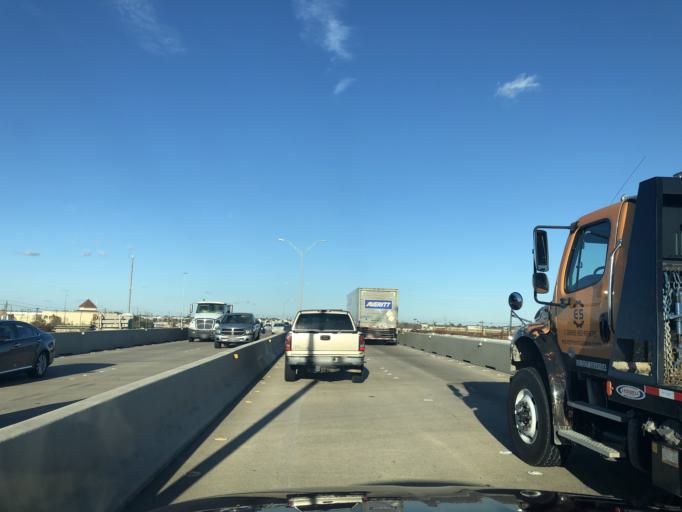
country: US
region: Texas
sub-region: Harris County
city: Pasadena
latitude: 29.6387
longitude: -95.1609
